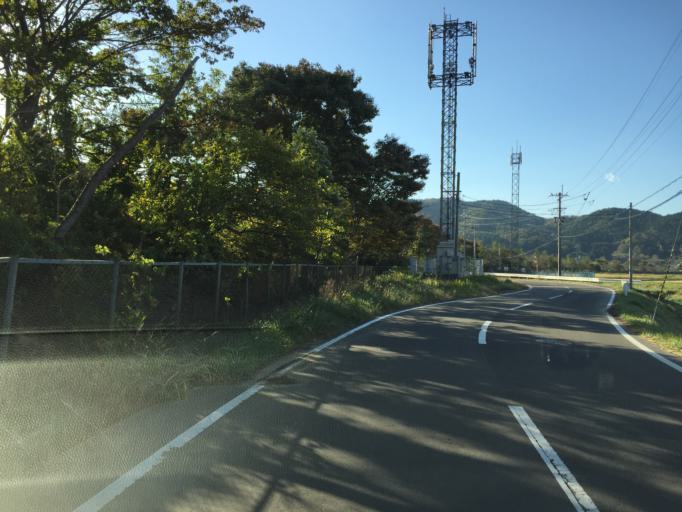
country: JP
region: Miyagi
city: Shiroishi
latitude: 37.9284
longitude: 140.6102
